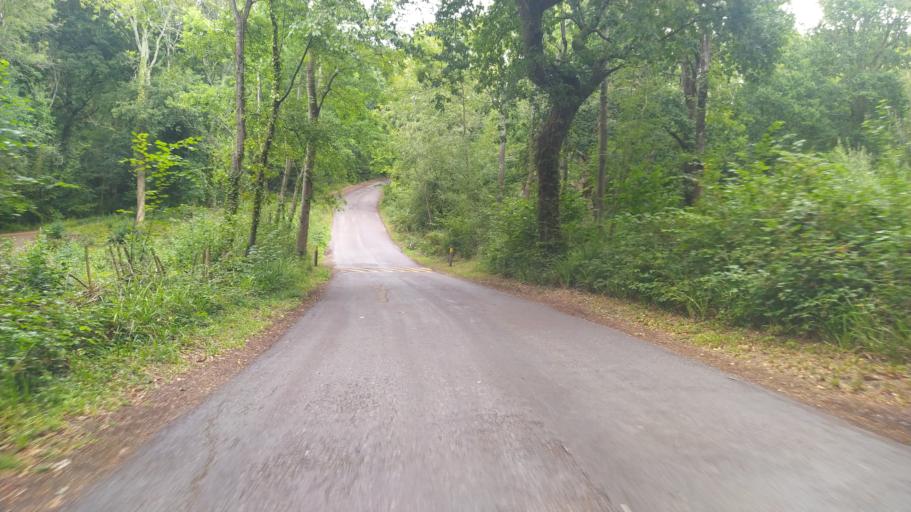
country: GB
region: England
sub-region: Hampshire
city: Hedge End
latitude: 50.8964
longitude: -1.2950
